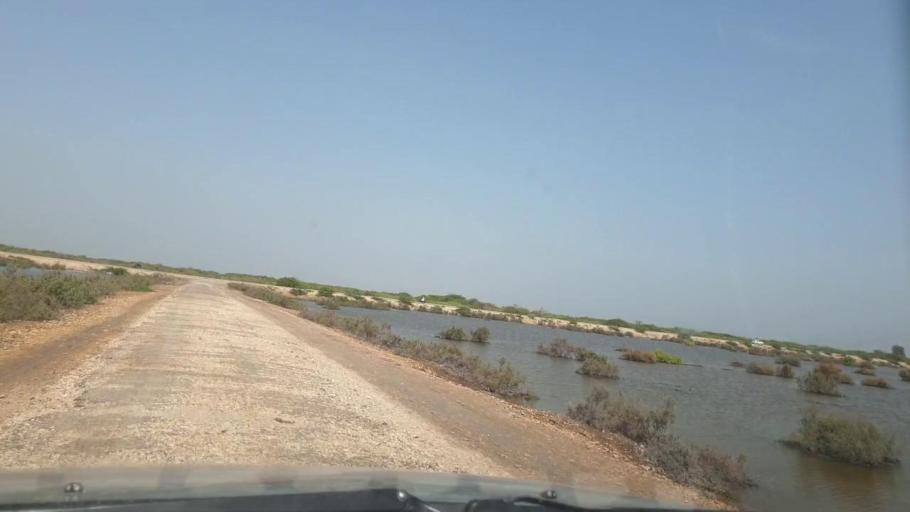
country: PK
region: Sindh
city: Tando Ghulam Ali
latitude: 25.1135
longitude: 68.8021
